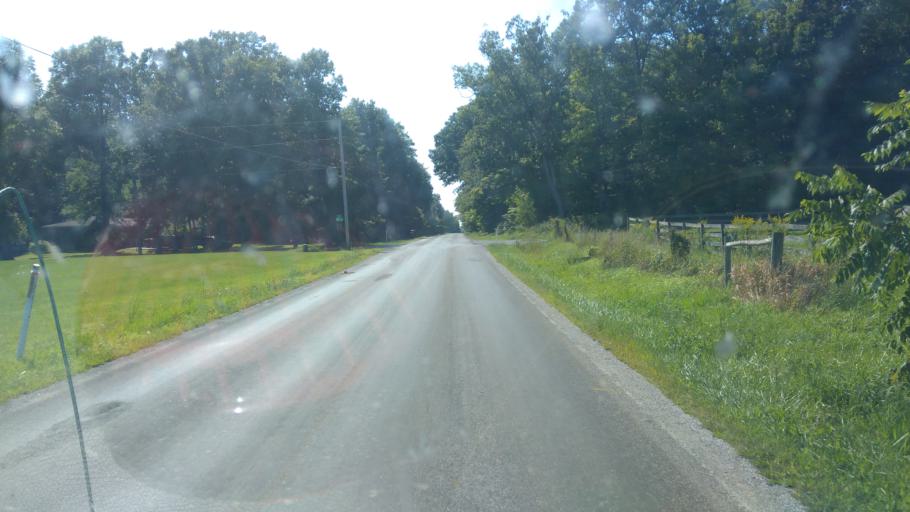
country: US
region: Ohio
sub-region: Ashland County
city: Ashland
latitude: 40.9700
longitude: -82.2909
